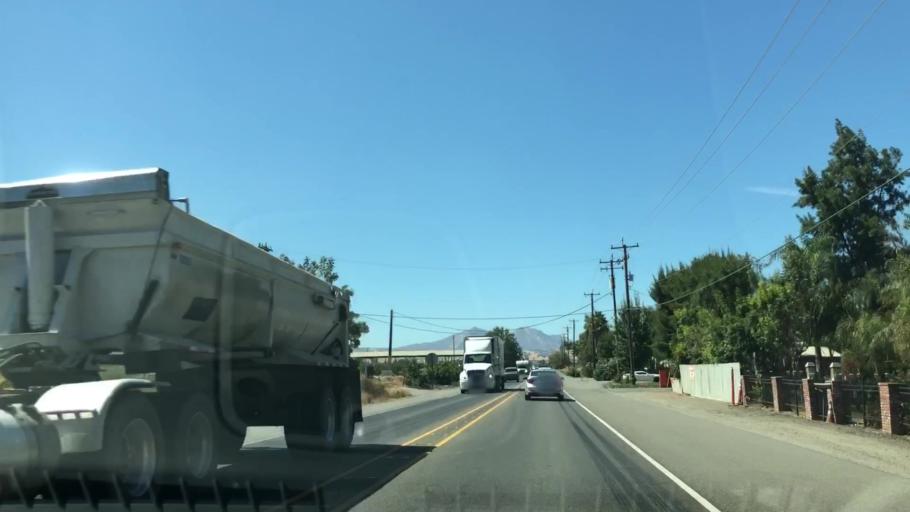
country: US
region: California
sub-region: Contra Costa County
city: Byron
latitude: 37.8965
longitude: -121.6660
